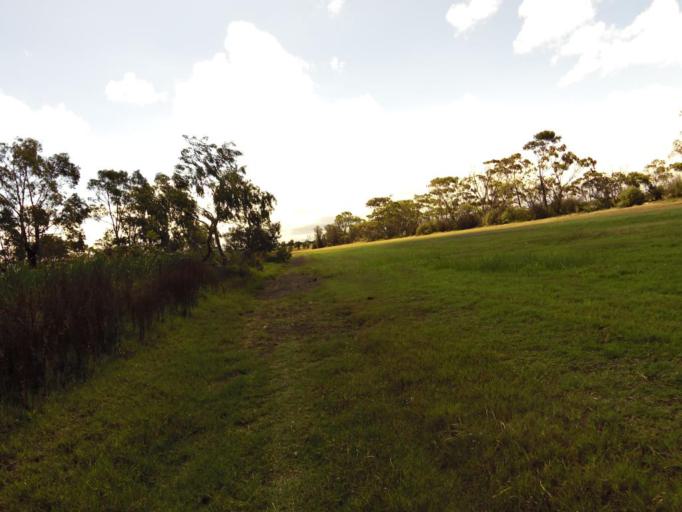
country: AU
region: Victoria
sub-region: Hobsons Bay
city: Laverton
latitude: -37.8632
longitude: 144.7840
